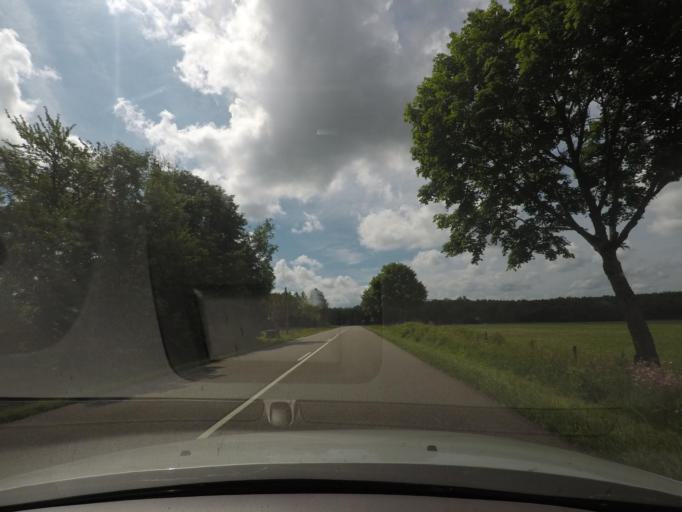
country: FR
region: Alsace
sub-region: Departement du Bas-Rhin
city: Sarrewerden
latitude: 48.8942
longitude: 7.1323
